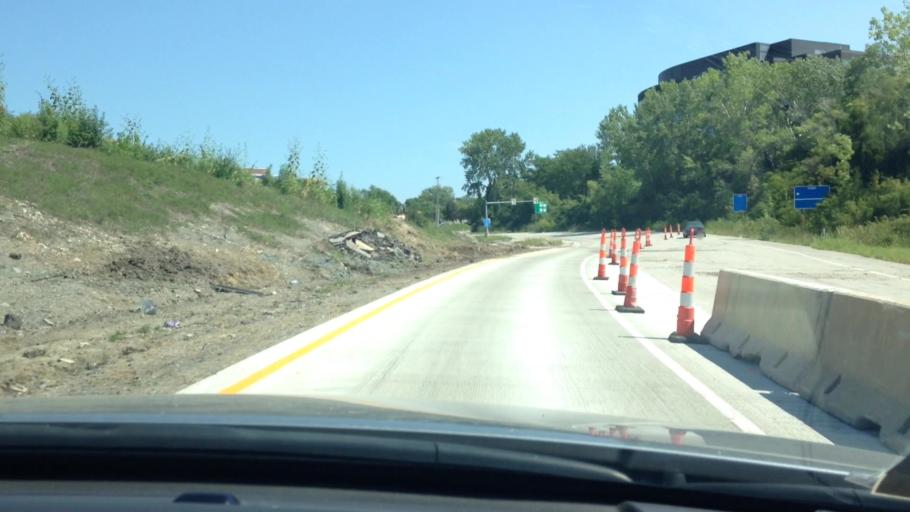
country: US
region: Kansas
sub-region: Johnson County
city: Leawood
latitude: 38.9401
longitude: -94.5852
